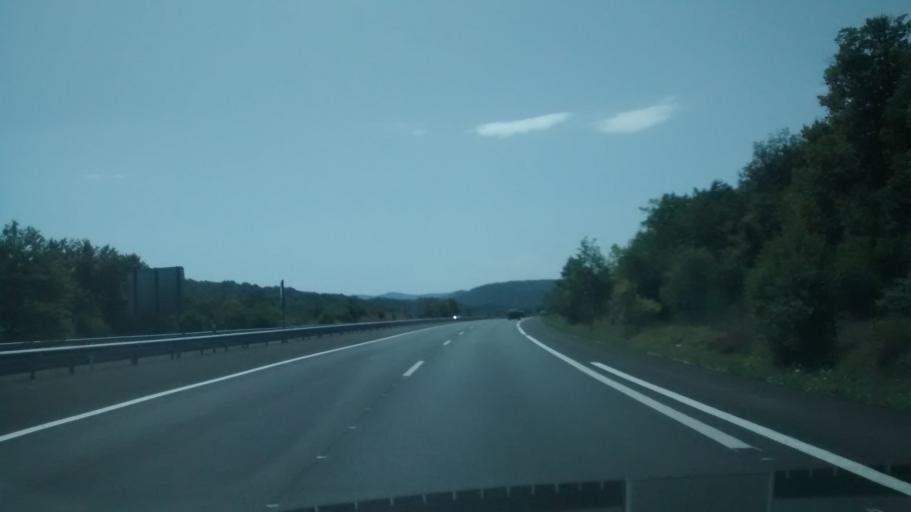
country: ES
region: Basque Country
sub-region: Provincia de Alava
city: Murguia
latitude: 42.9588
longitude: -2.8707
